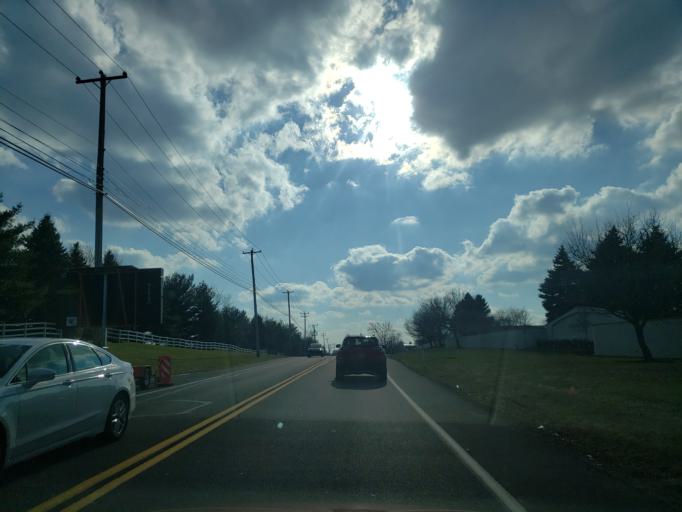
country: US
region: Pennsylvania
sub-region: Montgomery County
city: North Wales
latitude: 40.1823
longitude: -75.2755
